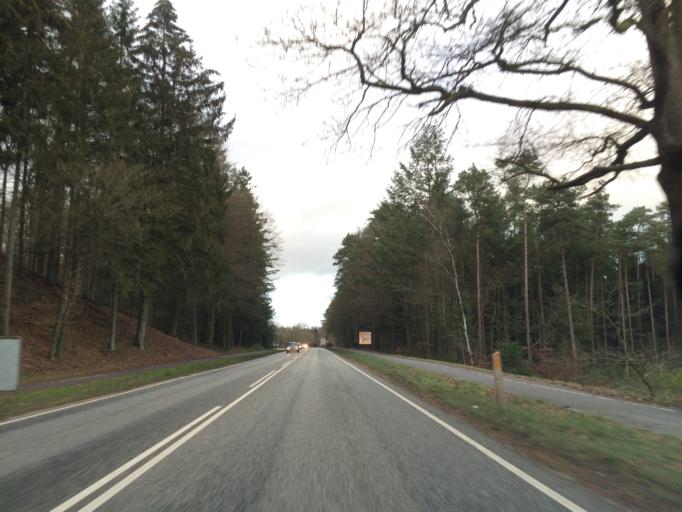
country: DK
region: Central Jutland
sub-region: Silkeborg Kommune
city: Silkeborg
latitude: 56.1519
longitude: 9.5515
